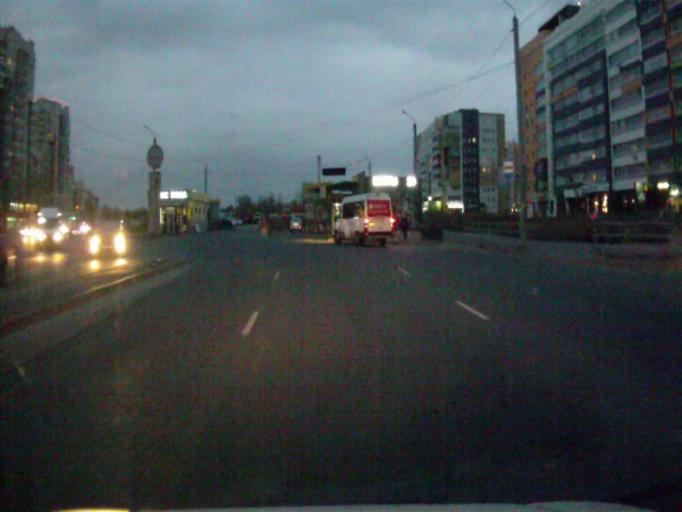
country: RU
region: Chelyabinsk
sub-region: Gorod Chelyabinsk
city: Chelyabinsk
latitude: 55.1627
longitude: 61.2949
